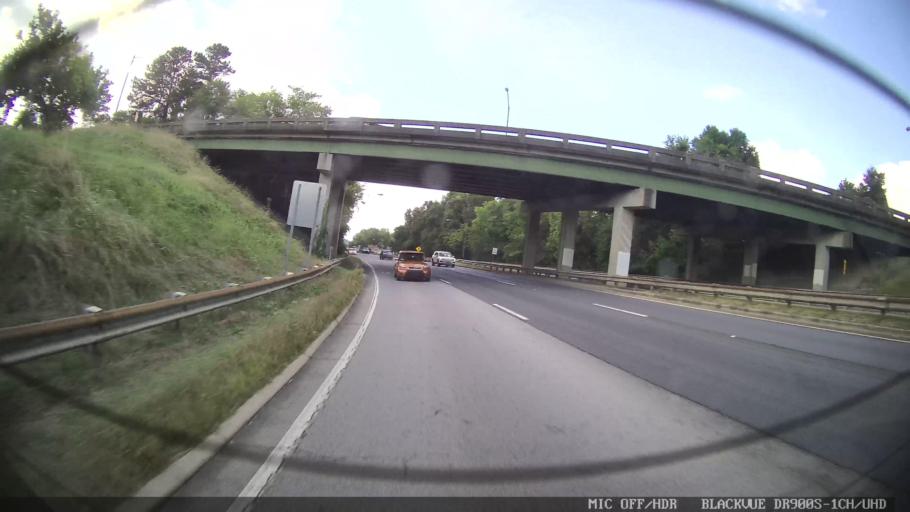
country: US
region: Georgia
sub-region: Floyd County
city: Rome
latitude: 34.2371
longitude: -85.1610
